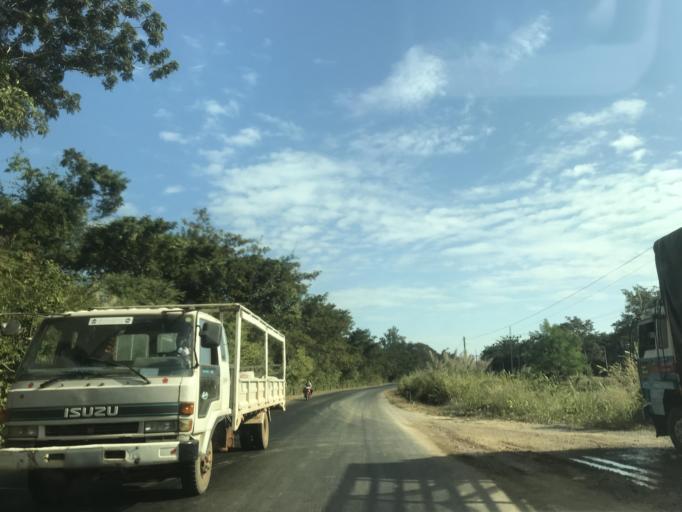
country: LA
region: Khammouan
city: Muang Hinboun
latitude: 17.7947
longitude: 104.4898
